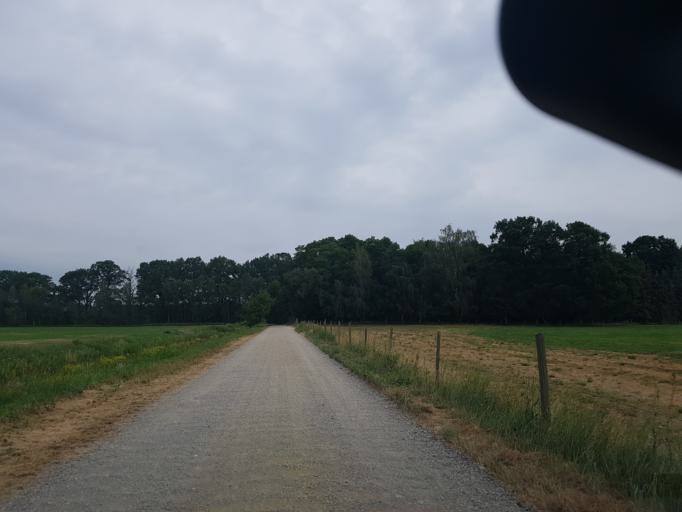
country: DE
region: Brandenburg
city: Schonewalde
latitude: 51.6995
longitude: 13.5410
